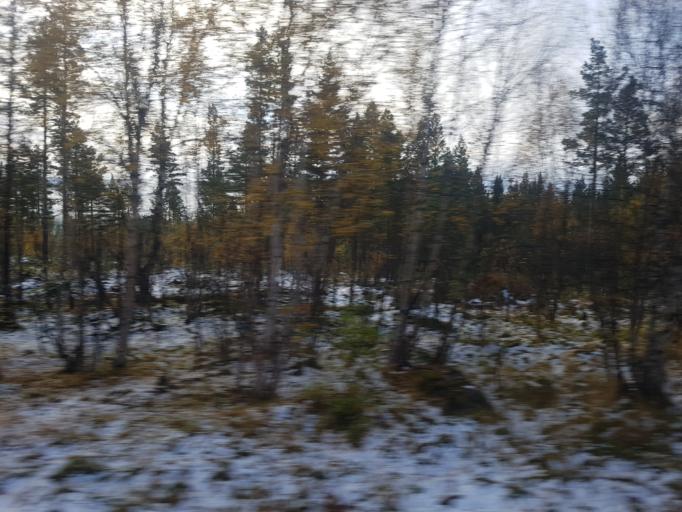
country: NO
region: Sor-Trondelag
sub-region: Oppdal
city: Oppdal
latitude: 62.6240
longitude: 9.7724
